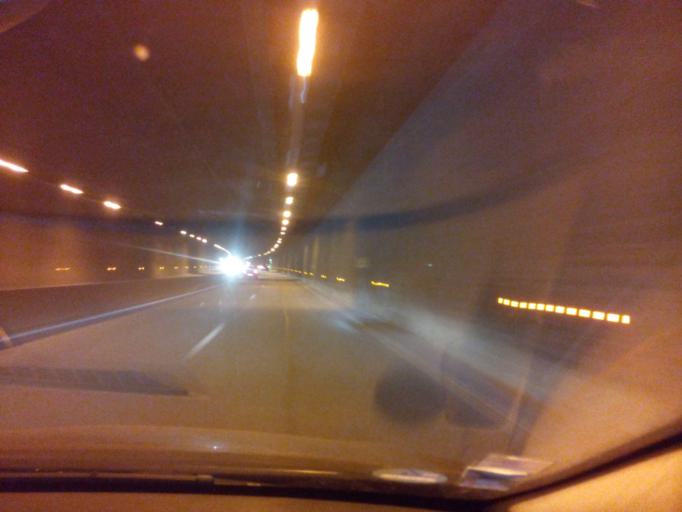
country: FR
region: Ile-de-France
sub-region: Departement des Hauts-de-Seine
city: Antony
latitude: 48.7620
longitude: 2.3010
